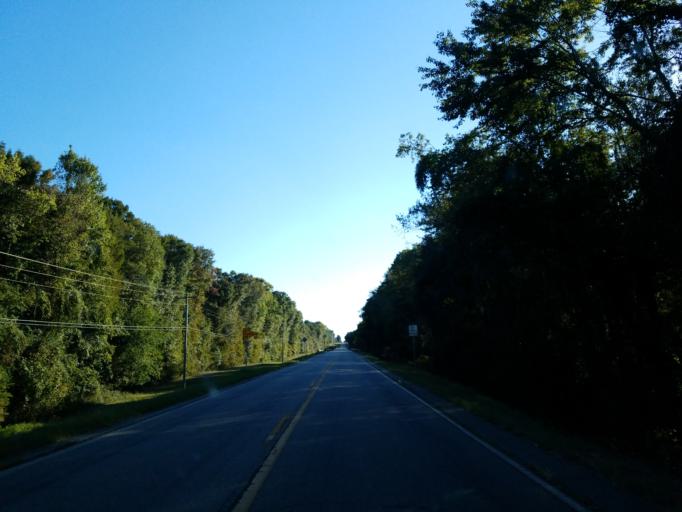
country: US
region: Georgia
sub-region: Lee County
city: Leesburg
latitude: 31.7794
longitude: -84.1370
